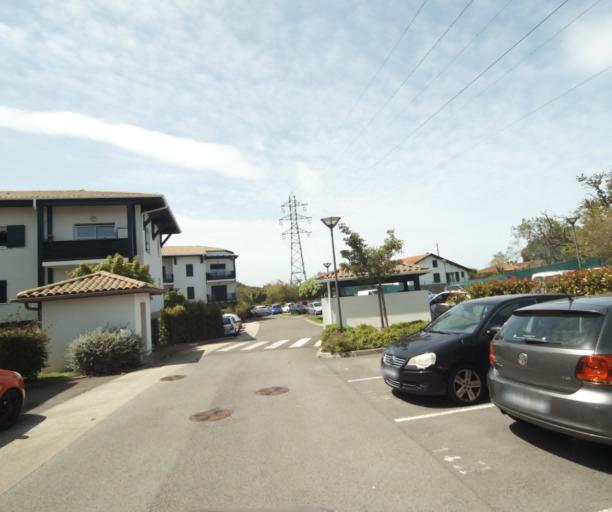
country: FR
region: Aquitaine
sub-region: Departement des Pyrenees-Atlantiques
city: Mouguerre
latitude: 43.4654
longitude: -1.4423
